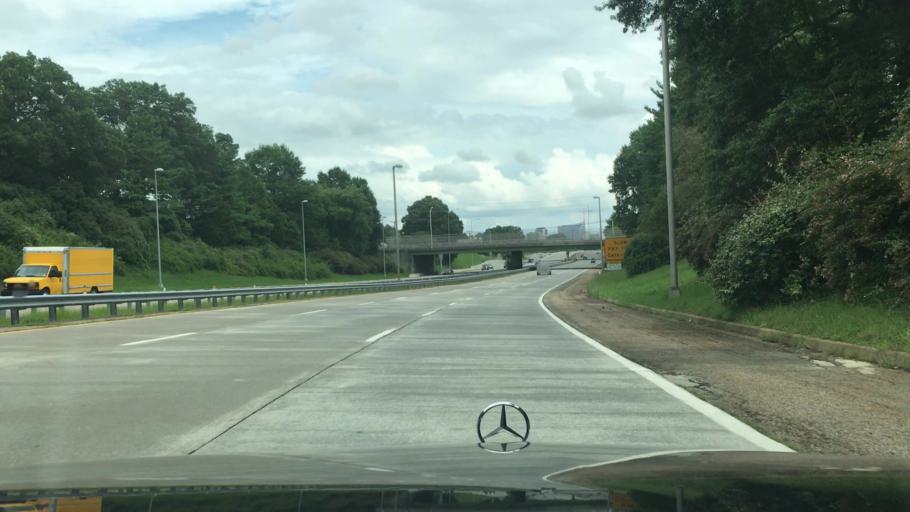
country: US
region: Virginia
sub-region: City of Richmond
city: Richmond
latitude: 37.5476
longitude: -77.4694
